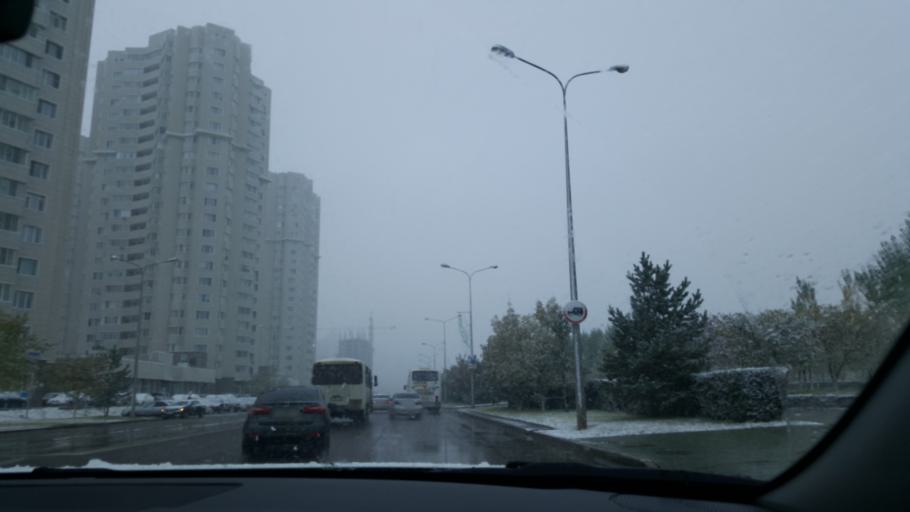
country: KZ
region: Astana Qalasy
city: Astana
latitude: 51.1201
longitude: 71.4670
